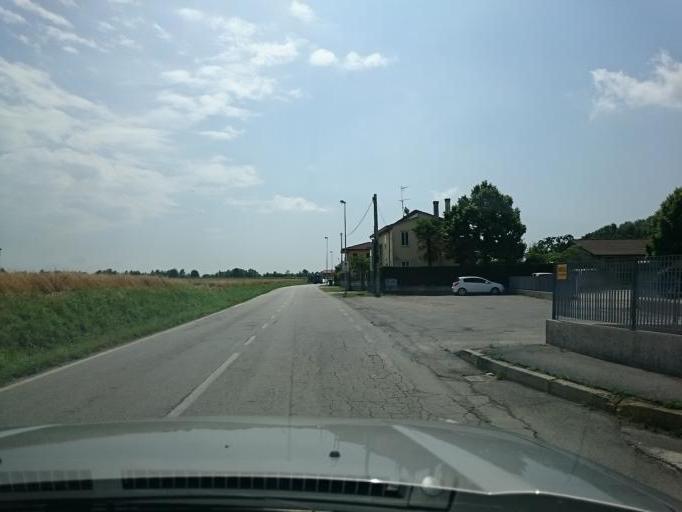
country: IT
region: Veneto
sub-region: Provincia di Padova
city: Terradura
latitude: 45.3462
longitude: 11.8353
